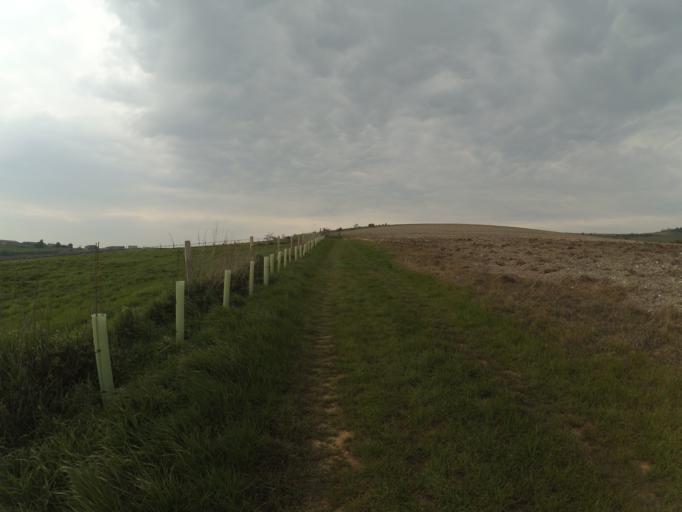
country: GB
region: England
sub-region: West Sussex
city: Arundel
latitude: 50.8969
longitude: -0.5214
